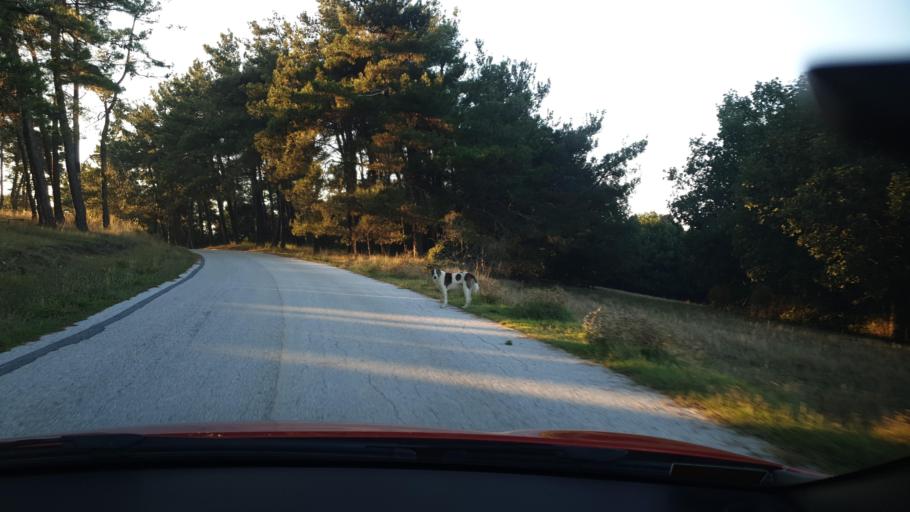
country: GR
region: Central Macedonia
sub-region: Nomos Thessalonikis
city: Peristera
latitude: 40.5109
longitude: 23.2193
